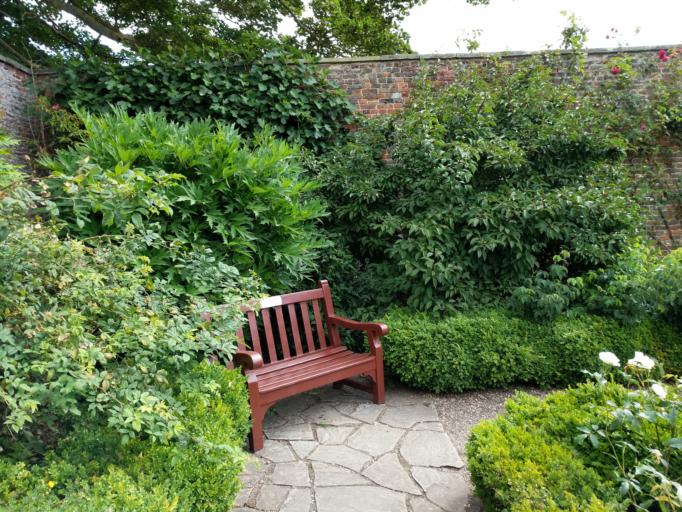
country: GB
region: England
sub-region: East Riding of Yorkshire
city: Bempton
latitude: 54.1048
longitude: -0.1579
